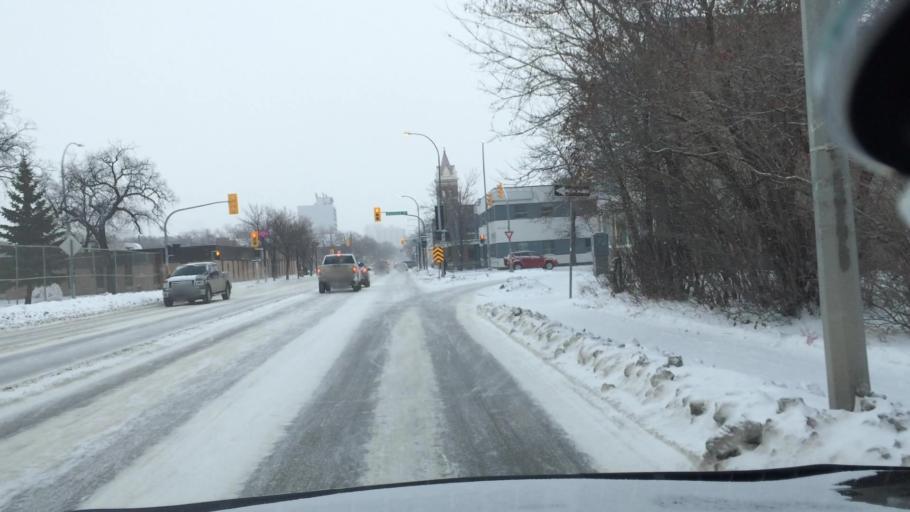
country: CA
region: Manitoba
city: Winnipeg
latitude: 49.8859
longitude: -97.1617
